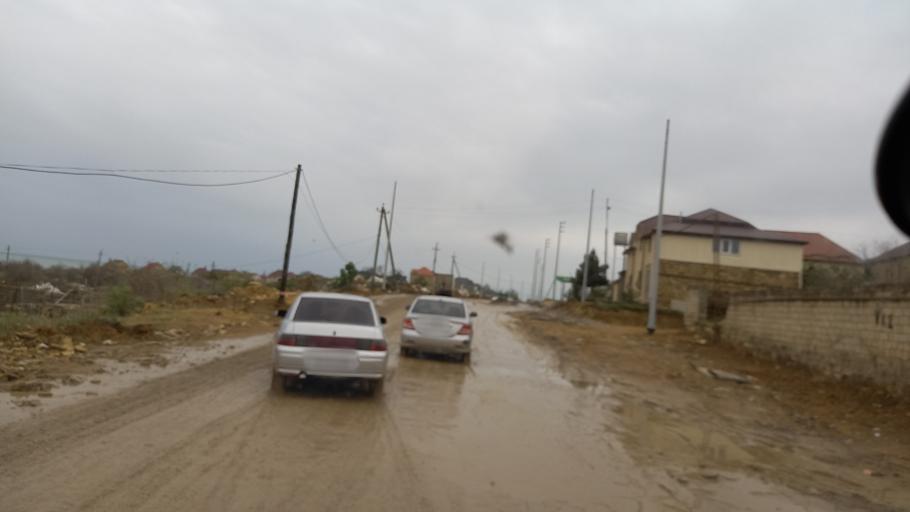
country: RU
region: Dagestan
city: Derbent
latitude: 42.1007
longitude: 48.2843
